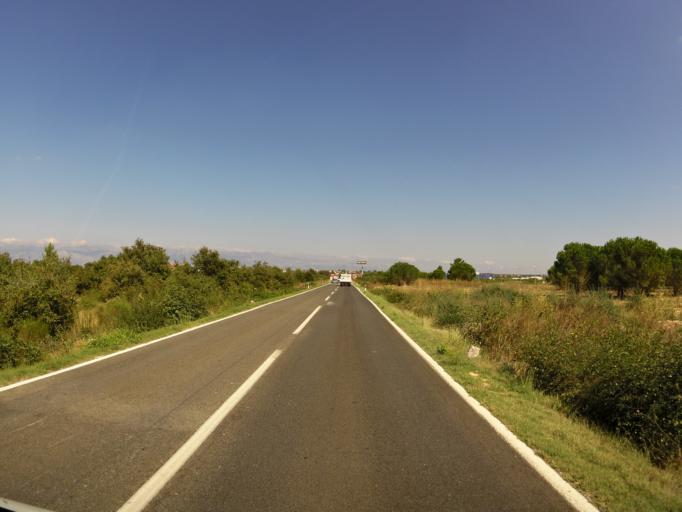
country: HR
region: Zadarska
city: Zadar
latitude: 44.1364
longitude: 15.3052
